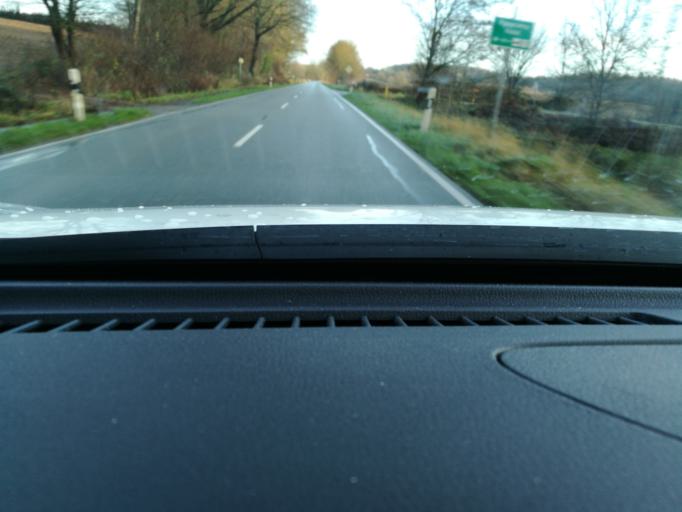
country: DE
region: Schleswig-Holstein
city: Ascheffel
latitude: 54.4118
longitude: 9.6978
